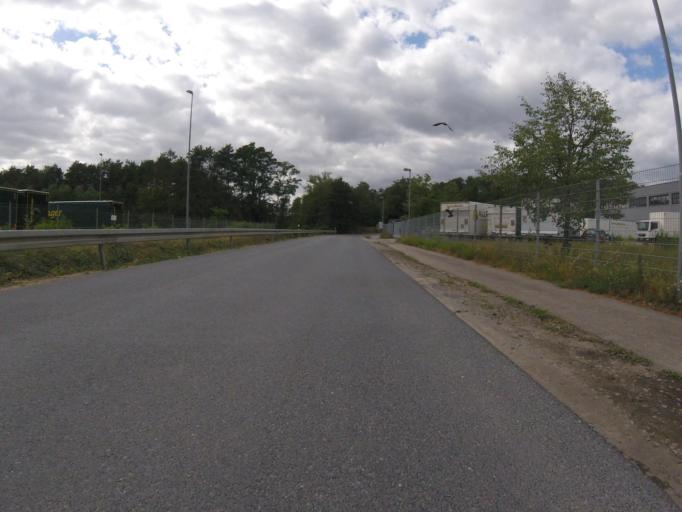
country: DE
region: Brandenburg
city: Wildau
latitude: 52.3182
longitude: 13.6712
